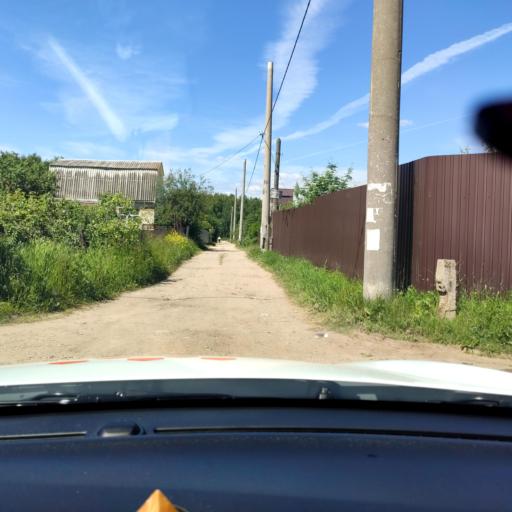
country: RU
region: Tatarstan
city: Vysokaya Gora
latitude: 55.8114
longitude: 49.2829
